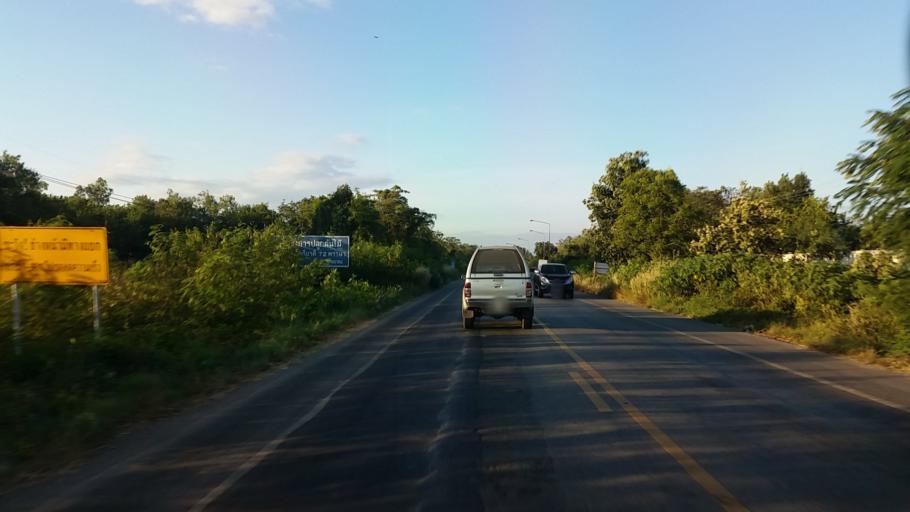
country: TH
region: Lop Buri
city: Chai Badan
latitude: 15.2521
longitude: 101.1754
